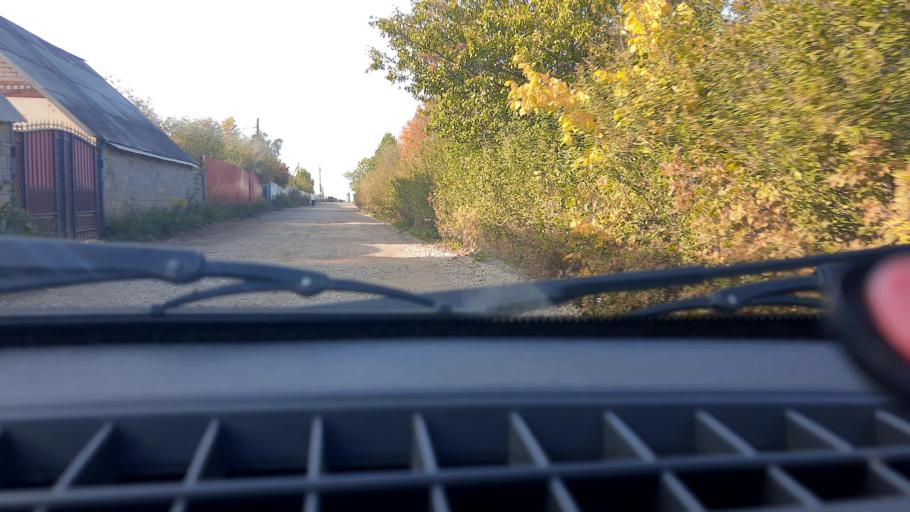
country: RU
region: Bashkortostan
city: Avdon
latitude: 54.5761
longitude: 55.7321
